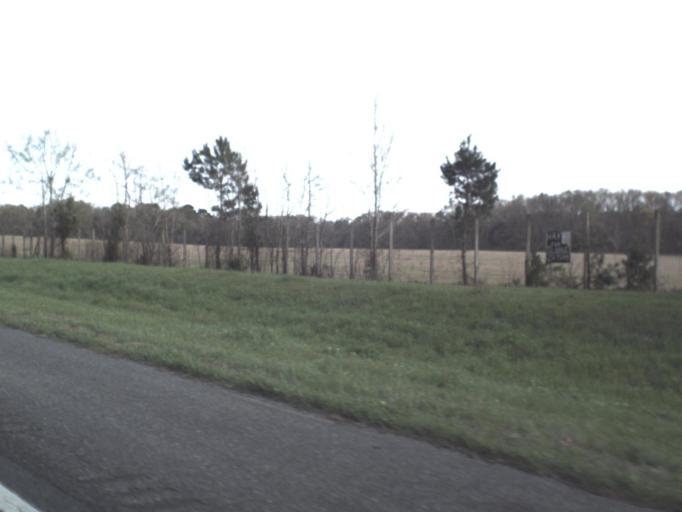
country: US
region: Florida
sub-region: Leon County
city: Tallahassee
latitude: 30.4781
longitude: -84.1195
